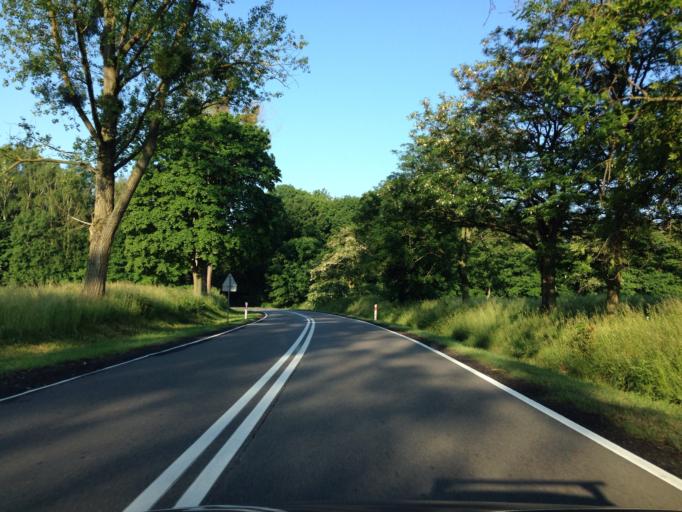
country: PL
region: Pomeranian Voivodeship
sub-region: Powiat kwidzynski
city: Gardeja
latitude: 53.5911
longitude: 18.9130
